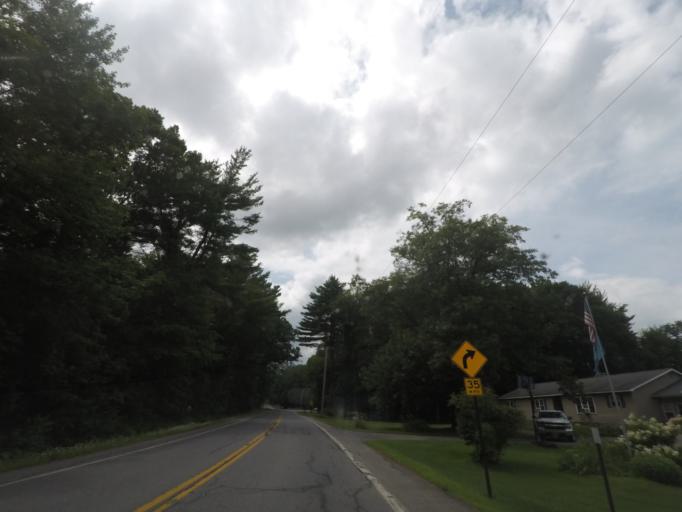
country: US
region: New York
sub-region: Saratoga County
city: Saratoga Springs
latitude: 43.0500
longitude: -73.6815
